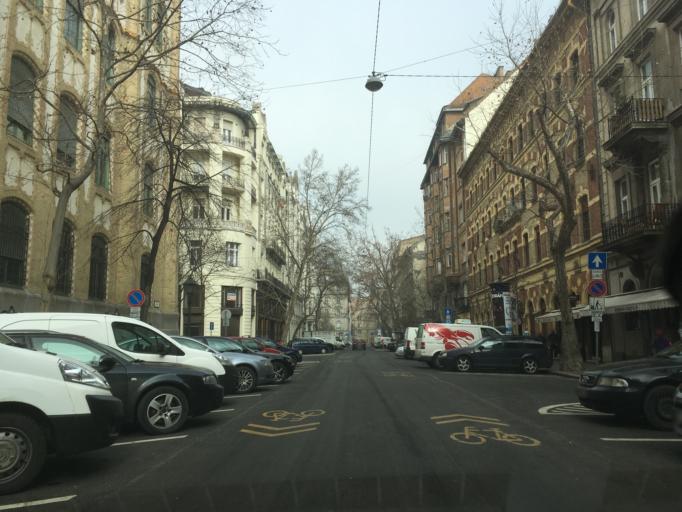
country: HU
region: Budapest
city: Budapest VI. keruelet
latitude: 47.5044
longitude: 19.0525
